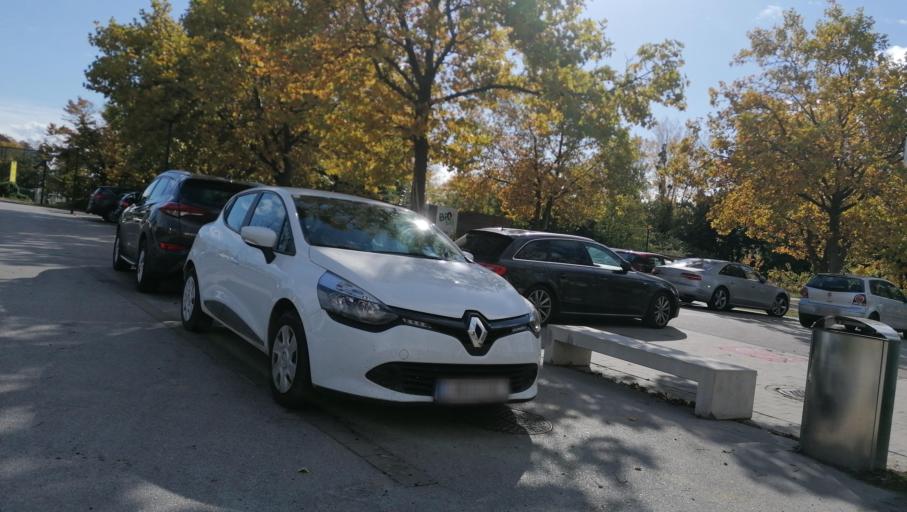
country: AT
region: Lower Austria
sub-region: Politischer Bezirk Baden
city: Tattendorf
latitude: 47.9581
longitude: 16.3008
